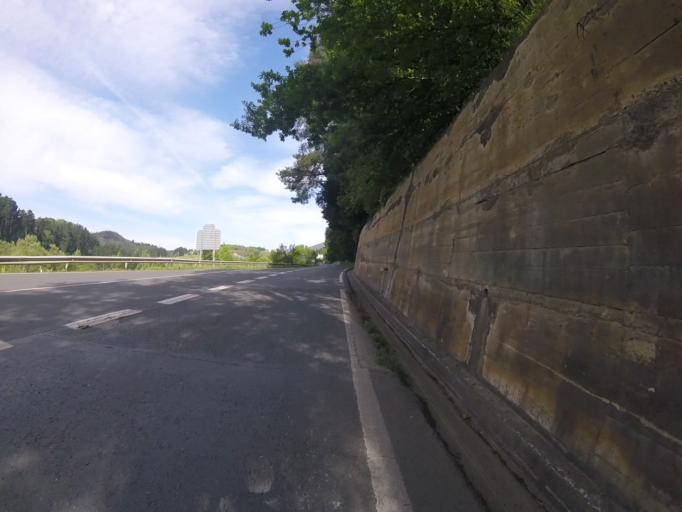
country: ES
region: Basque Country
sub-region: Provincia de Guipuzcoa
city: Zumarraga
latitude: 43.0817
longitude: -2.2992
